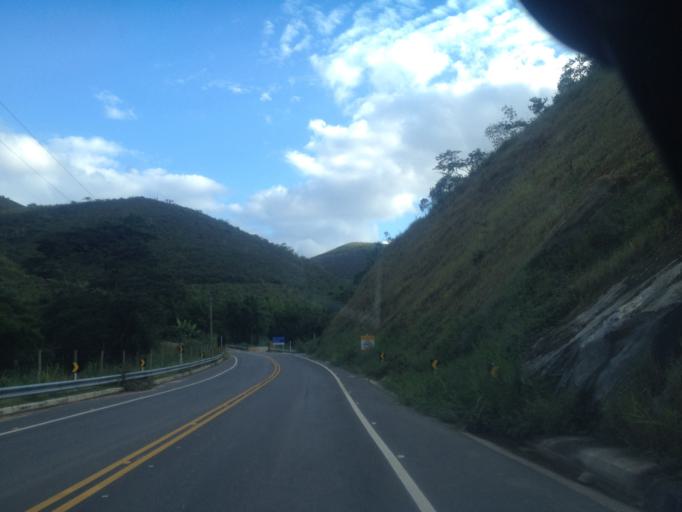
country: BR
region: Rio de Janeiro
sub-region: Quatis
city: Quatis
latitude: -22.2823
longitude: -44.2583
